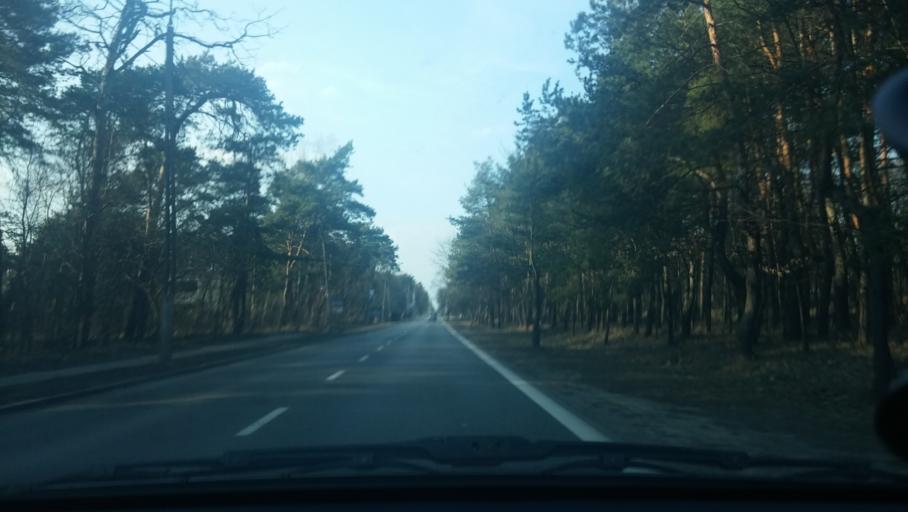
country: PL
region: Masovian Voivodeship
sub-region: Warszawa
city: Wawer
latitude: 52.1765
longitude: 21.1960
